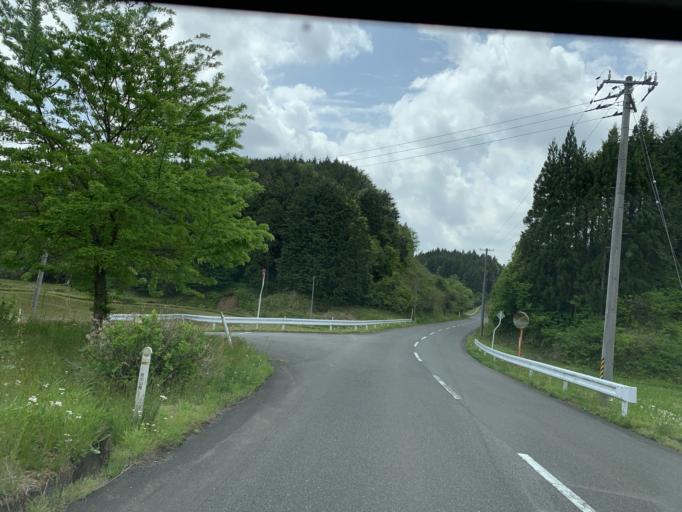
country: JP
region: Miyagi
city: Furukawa
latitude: 38.7150
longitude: 140.9206
